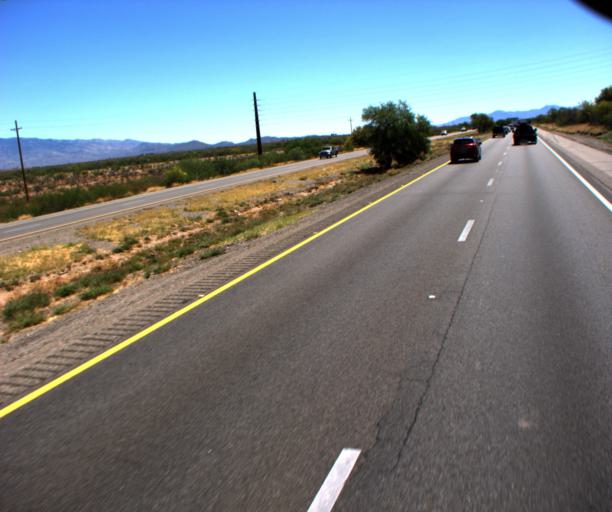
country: US
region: Arizona
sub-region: Pima County
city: Vail
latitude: 32.0771
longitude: -110.7987
